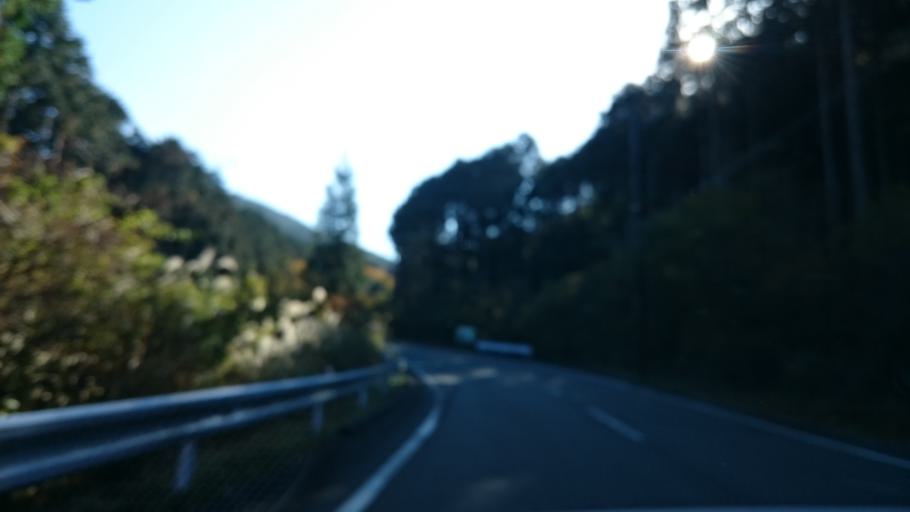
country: JP
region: Shizuoka
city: Heda
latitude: 34.9915
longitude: 138.8113
